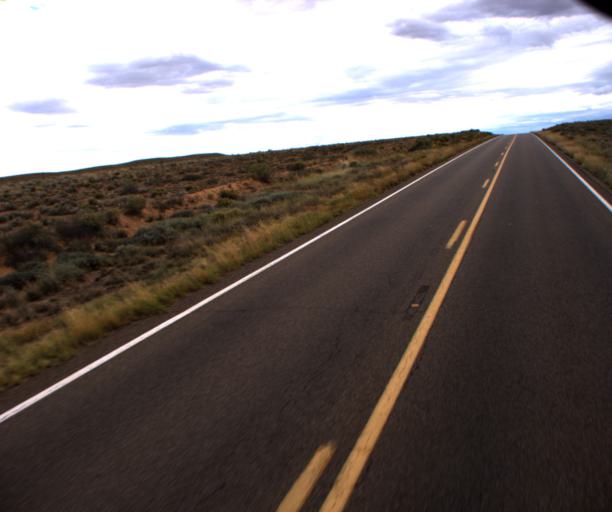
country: US
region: Arizona
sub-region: Navajo County
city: Holbrook
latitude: 34.8294
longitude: -110.1431
